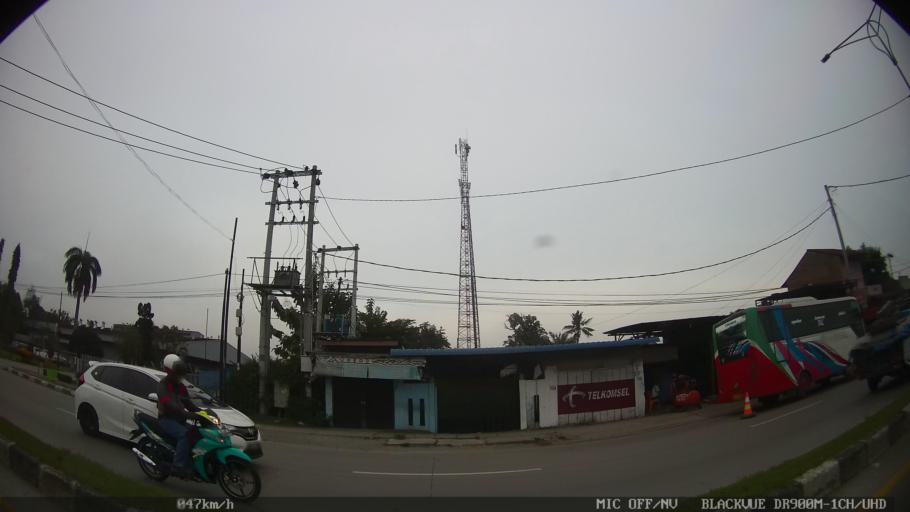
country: ID
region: North Sumatra
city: Deli Tua
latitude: 3.5324
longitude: 98.7277
